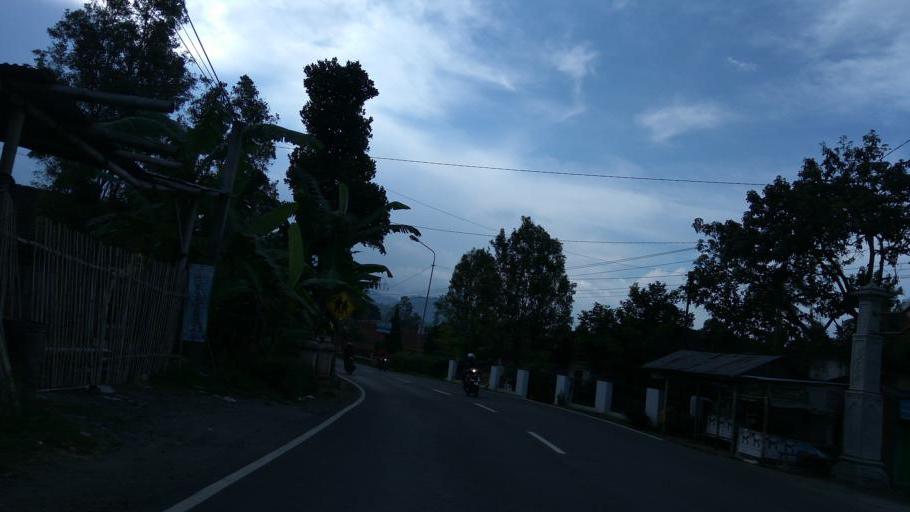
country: ID
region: Central Java
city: Salatiga
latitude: -7.3670
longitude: 110.4681
